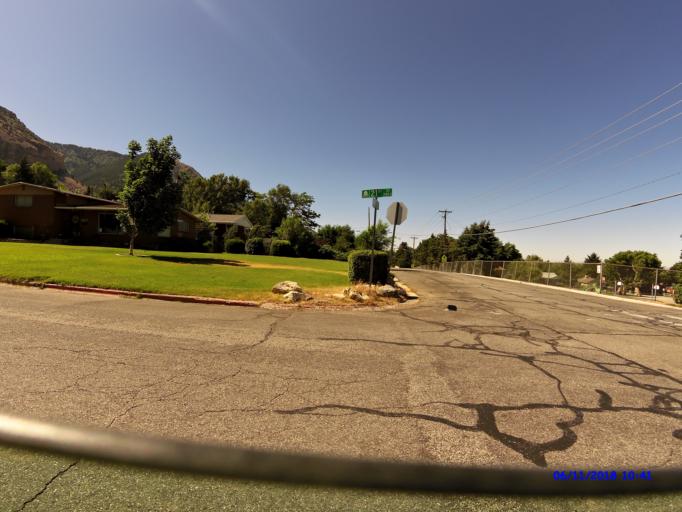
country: US
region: Utah
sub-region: Weber County
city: Ogden
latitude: 41.2286
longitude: -111.9369
